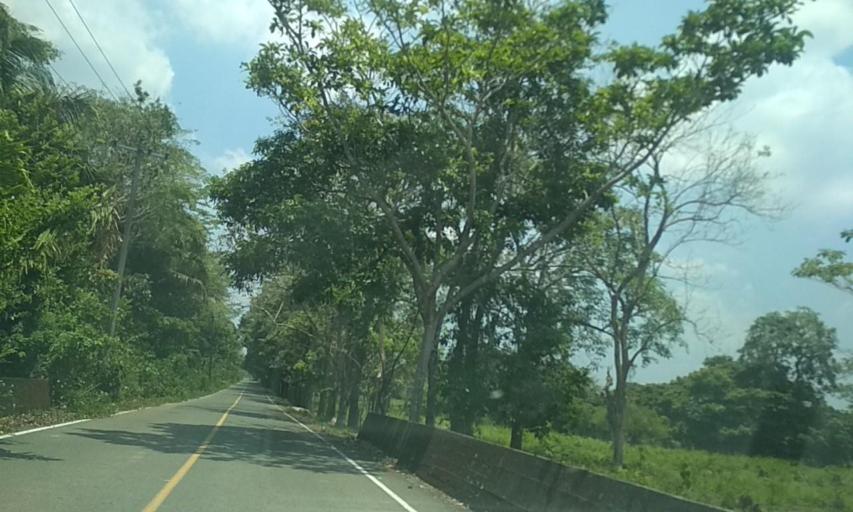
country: MX
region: Tabasco
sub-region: Huimanguillo
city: Francisco Rueda
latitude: 17.7549
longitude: -94.0289
